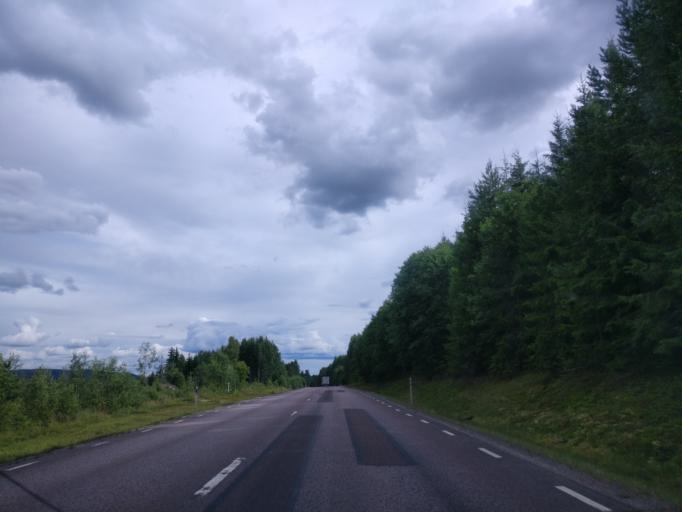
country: SE
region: Vaermland
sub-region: Hagfors Kommun
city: Ekshaerad
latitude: 60.1500
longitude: 13.5197
